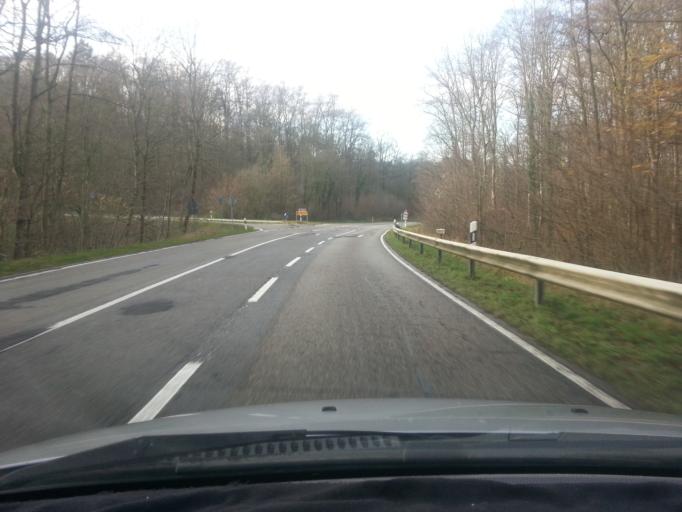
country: DE
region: Baden-Wuerttemberg
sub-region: Karlsruhe Region
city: Balzfeld
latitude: 49.1931
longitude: 8.8188
